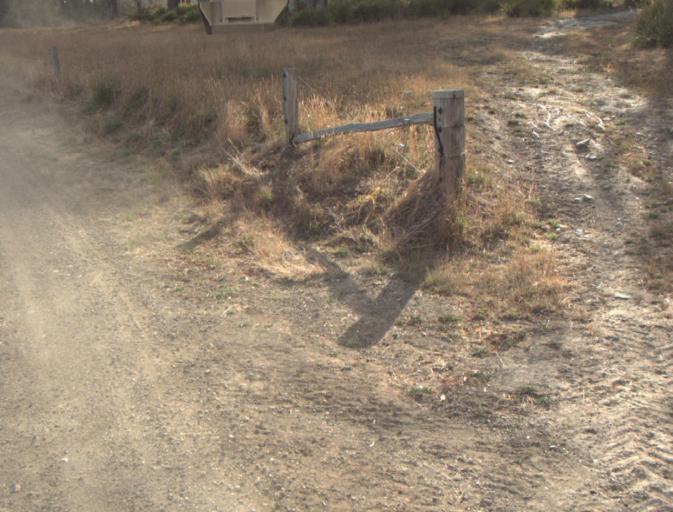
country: AU
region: Tasmania
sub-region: Dorset
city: Bridport
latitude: -41.1260
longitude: 147.2027
